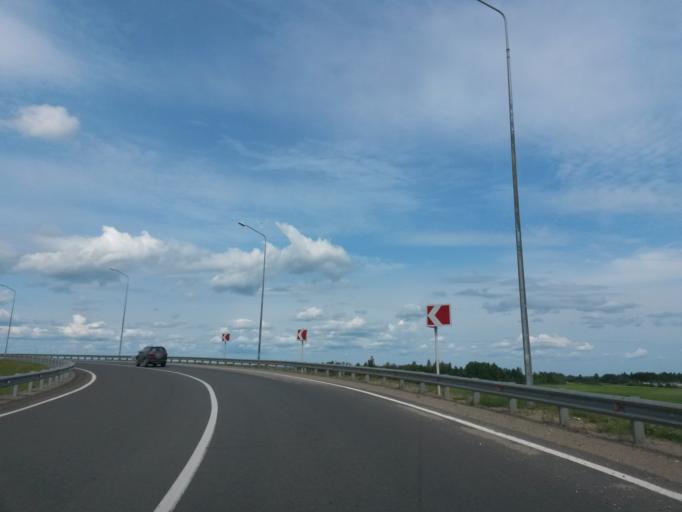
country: RU
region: Jaroslavl
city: Yaroslavl
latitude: 57.7382
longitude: 39.8999
